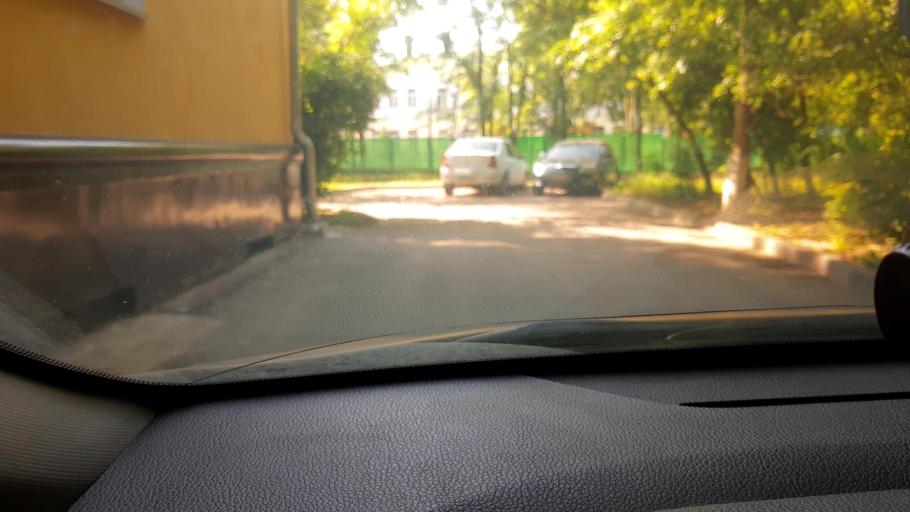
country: RU
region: Moskovskaya
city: Shcherbinka
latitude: 55.5137
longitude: 37.5702
